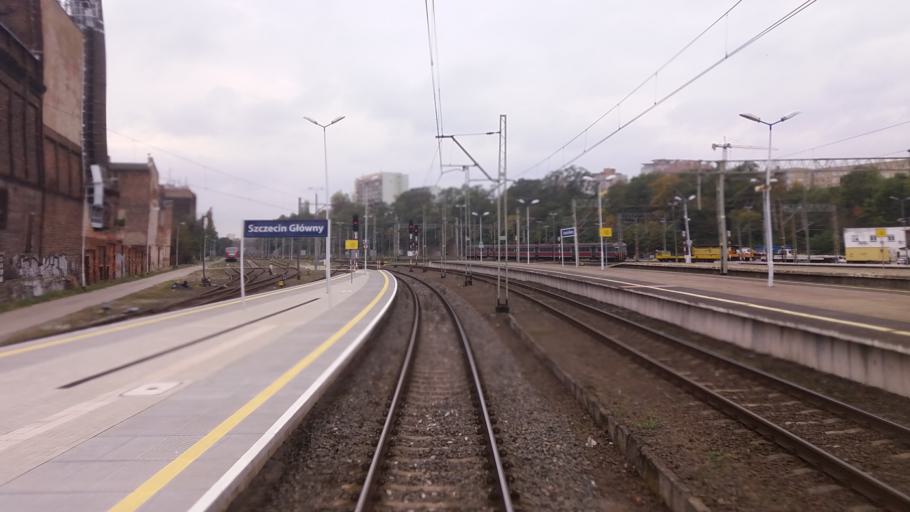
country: PL
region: West Pomeranian Voivodeship
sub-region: Szczecin
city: Szczecin
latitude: 53.4170
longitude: 14.5476
